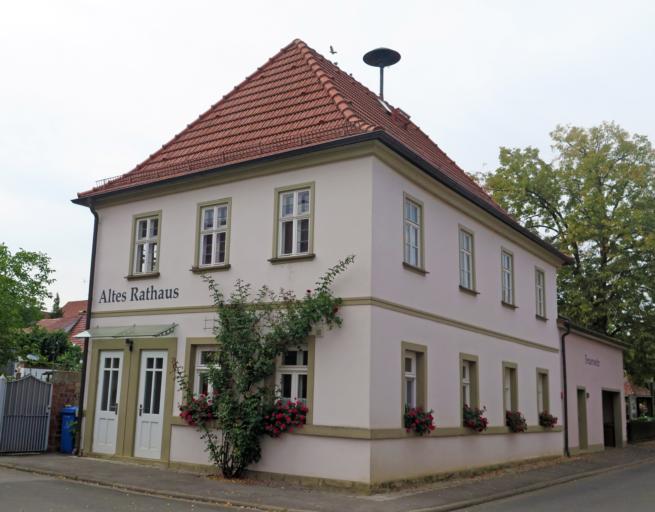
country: DE
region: Bavaria
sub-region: Regierungsbezirk Unterfranken
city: Hassfurt
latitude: 50.0714
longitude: 10.4799
